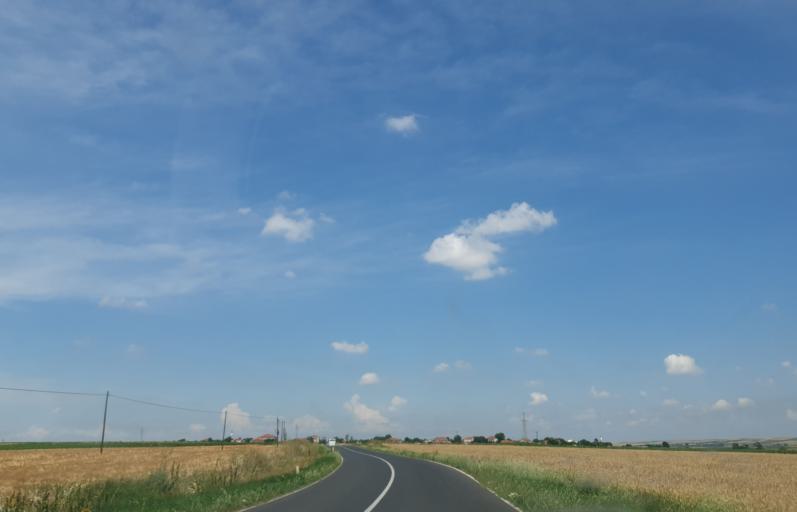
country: TR
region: Kirklareli
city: Buyukkaristiran
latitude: 41.2276
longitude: 27.5706
